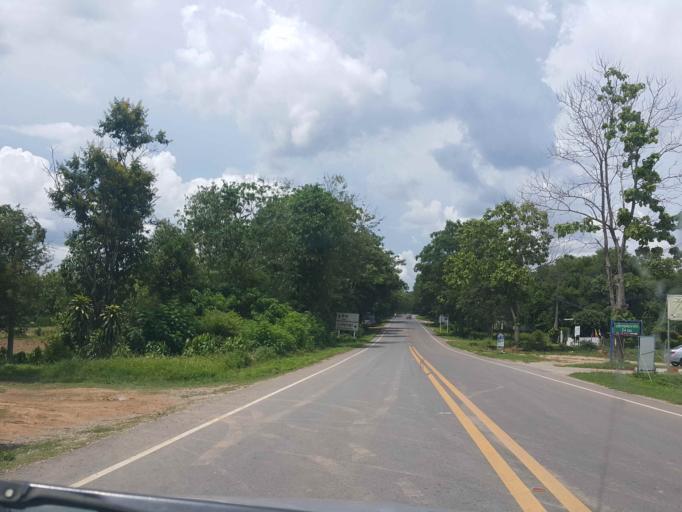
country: TH
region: Nan
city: Ban Luang
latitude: 18.8514
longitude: 100.4455
